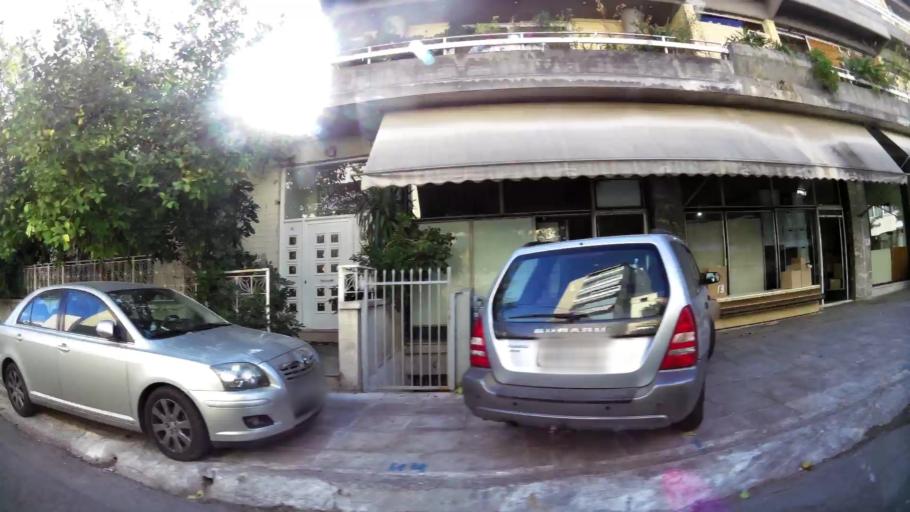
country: GR
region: Attica
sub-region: Nomos Piraios
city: Nikaia
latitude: 37.9709
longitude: 23.6560
